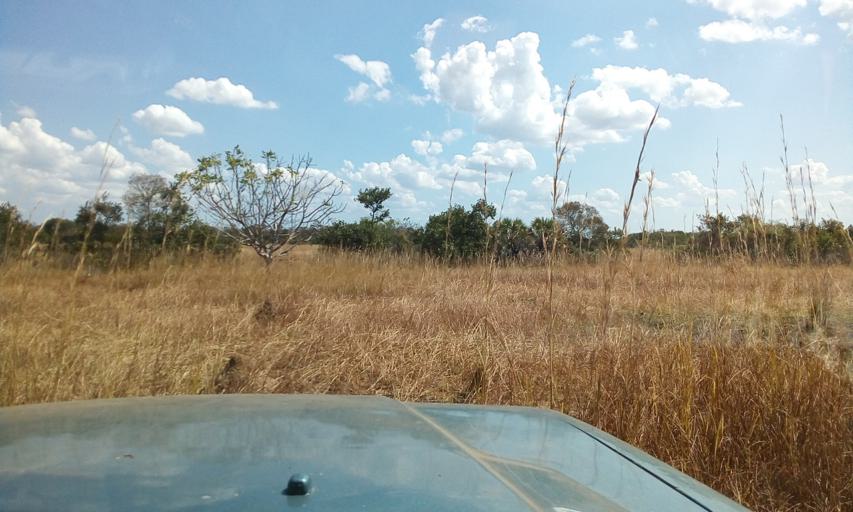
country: MG
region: Melaky
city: Mahabe
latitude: -16.4382
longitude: 45.3750
